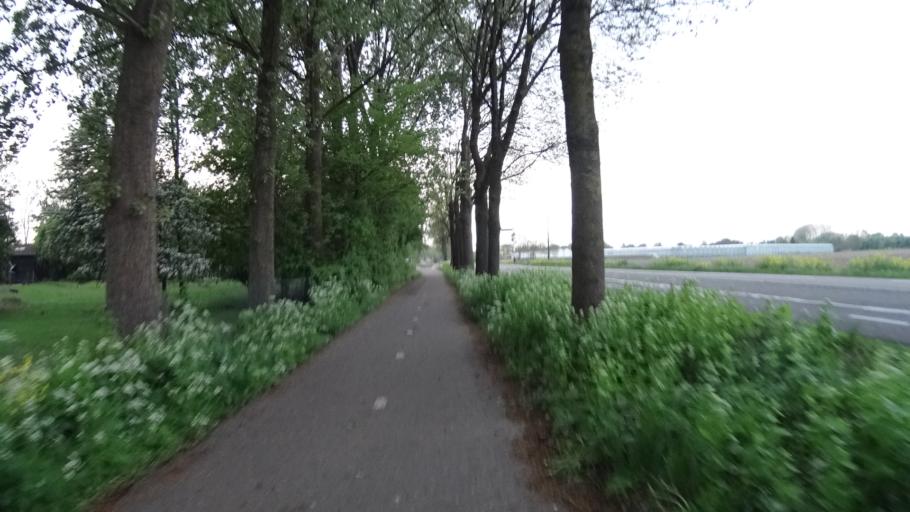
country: NL
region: North Brabant
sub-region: Gemeente Woudrichem
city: Woudrichem
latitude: 51.7833
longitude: 5.0375
